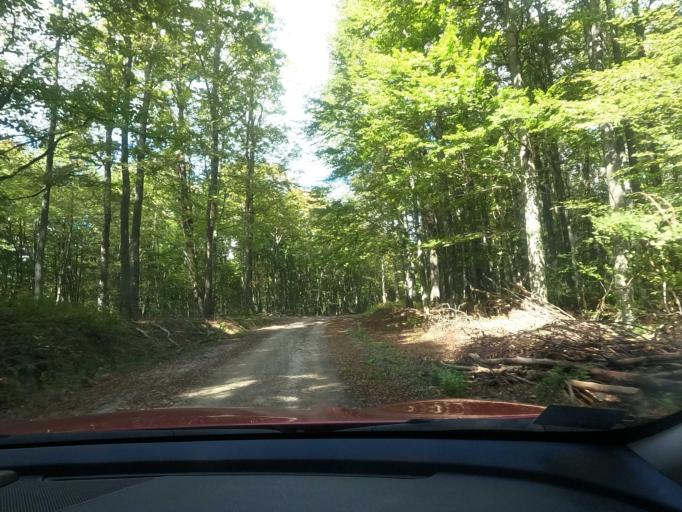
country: BA
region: Federation of Bosnia and Herzegovina
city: Velika Kladusa
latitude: 45.2499
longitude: 15.7696
